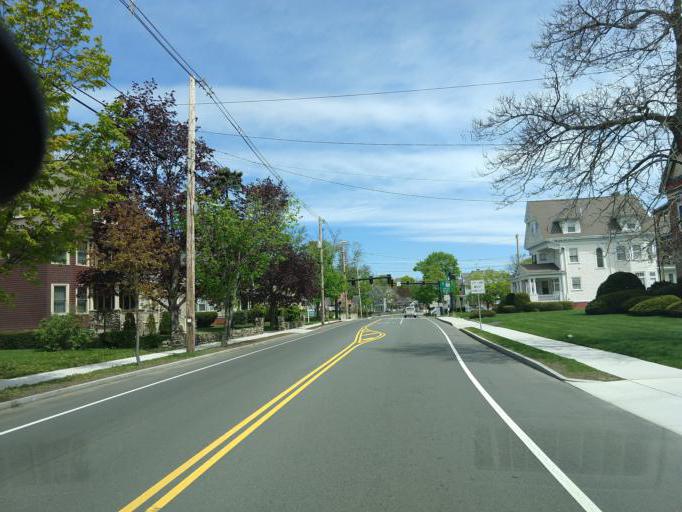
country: US
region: Massachusetts
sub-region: Essex County
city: Amesbury
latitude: 42.8502
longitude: -70.9376
